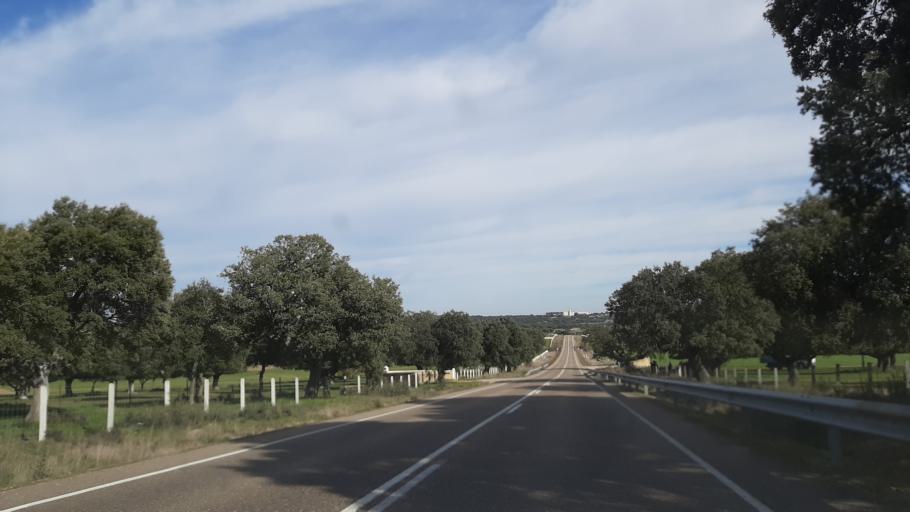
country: ES
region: Castille and Leon
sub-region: Provincia de Salamanca
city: Anover de Tormes
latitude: 41.0892
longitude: -5.9245
